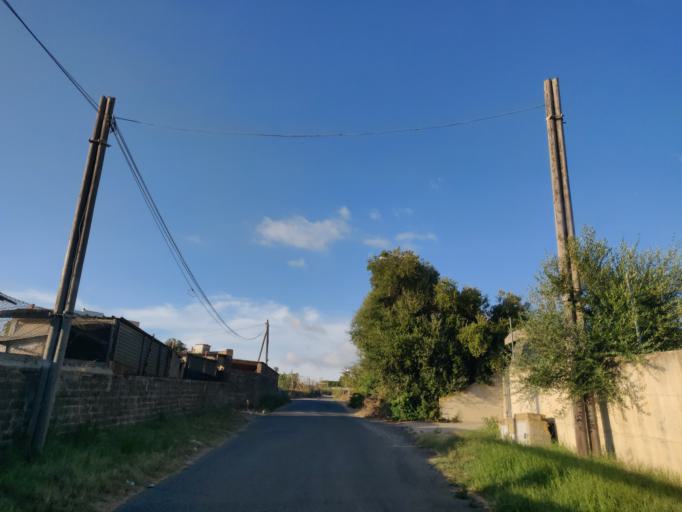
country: IT
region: Latium
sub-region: Citta metropolitana di Roma Capitale
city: Civitavecchia
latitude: 42.0932
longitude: 11.8183
